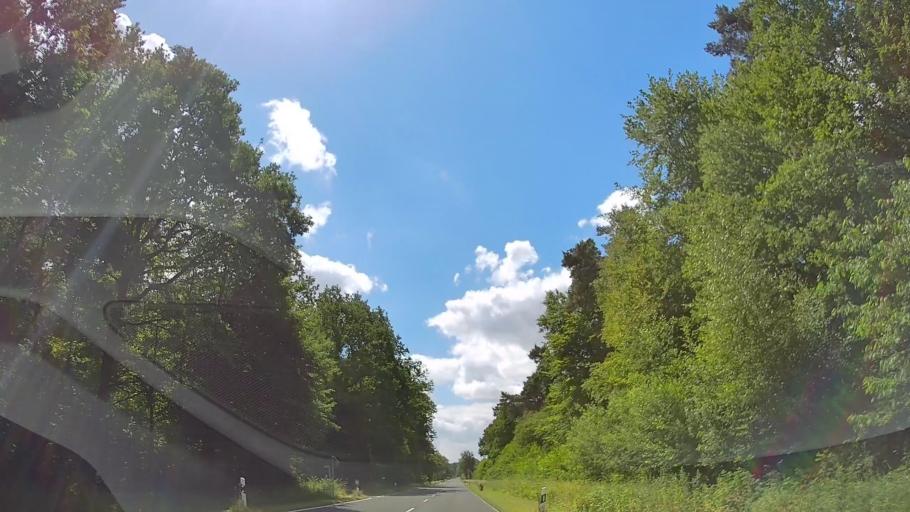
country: DE
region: North Rhine-Westphalia
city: Preussisch Oldendorf
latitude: 52.3965
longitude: 8.5204
